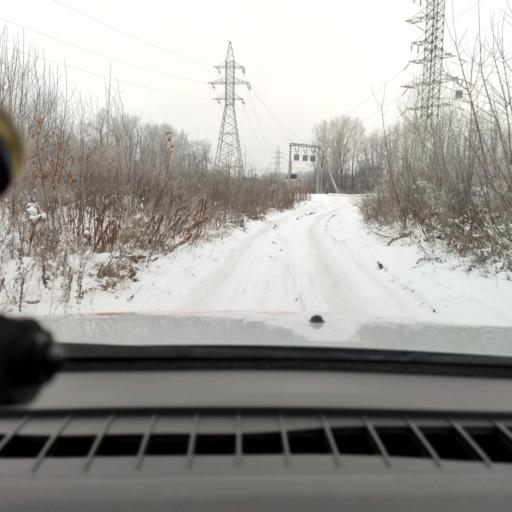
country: RU
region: Samara
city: Samara
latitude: 53.1451
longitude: 50.1859
